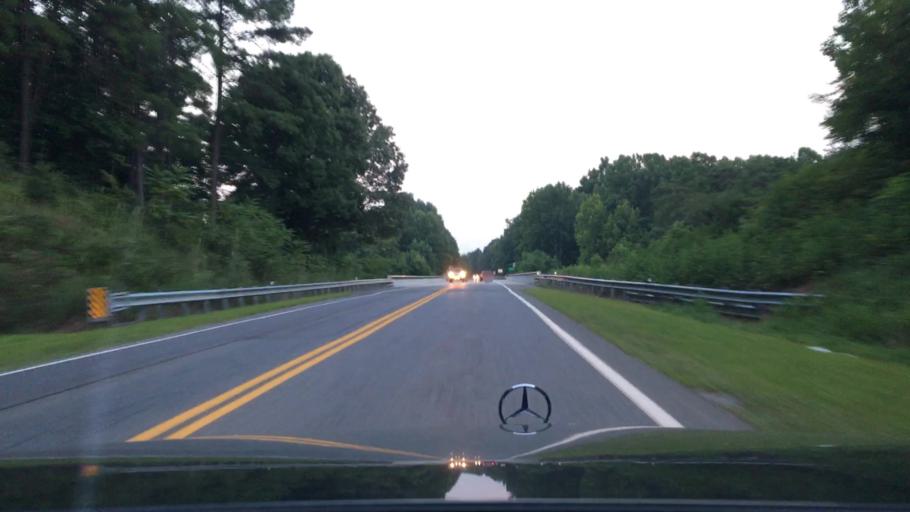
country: US
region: Virginia
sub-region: Campbell County
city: Altavista
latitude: 37.1368
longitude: -79.2910
